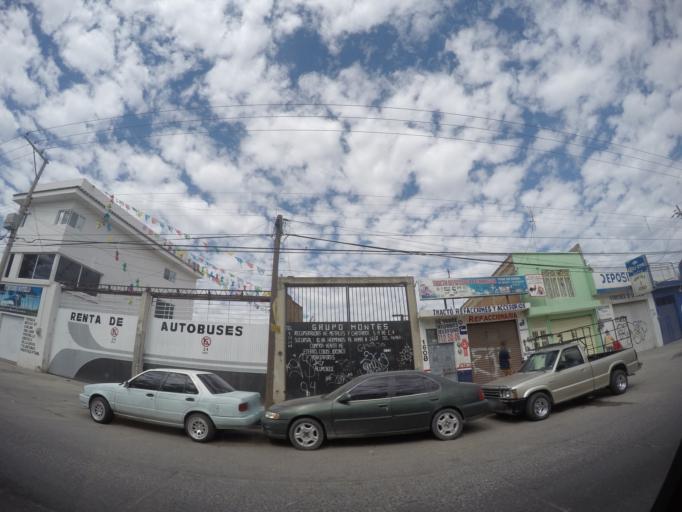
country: MX
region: Guanajuato
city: Leon
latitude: 21.0980
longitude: -101.6794
